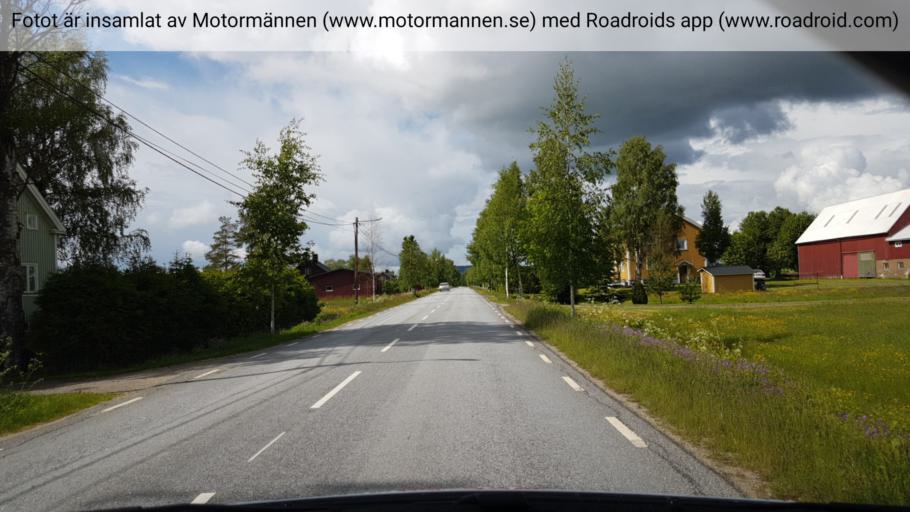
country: SE
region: Vaesterbotten
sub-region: Vannas Kommun
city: Vannasby
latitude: 63.9085
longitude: 19.8569
